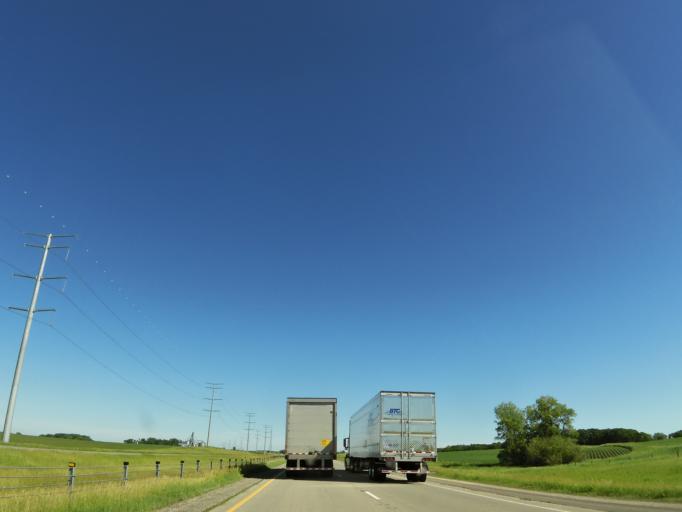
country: US
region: Minnesota
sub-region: Otter Tail County
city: Fergus Falls
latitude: 46.3861
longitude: -96.1871
